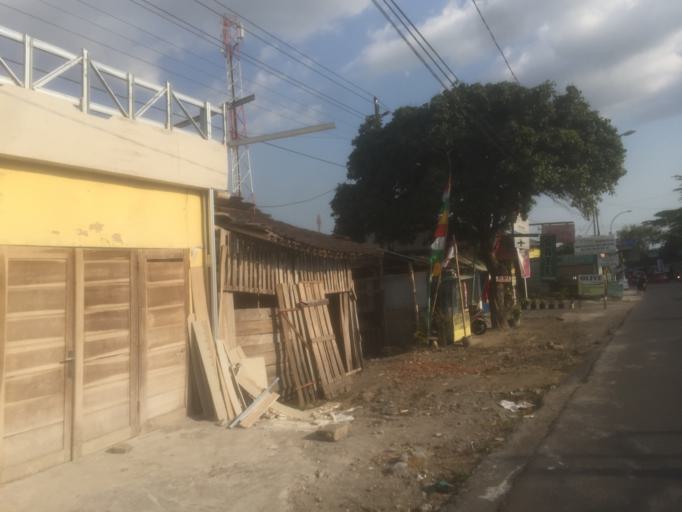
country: ID
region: Daerah Istimewa Yogyakarta
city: Sleman
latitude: -7.6835
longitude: 110.4194
